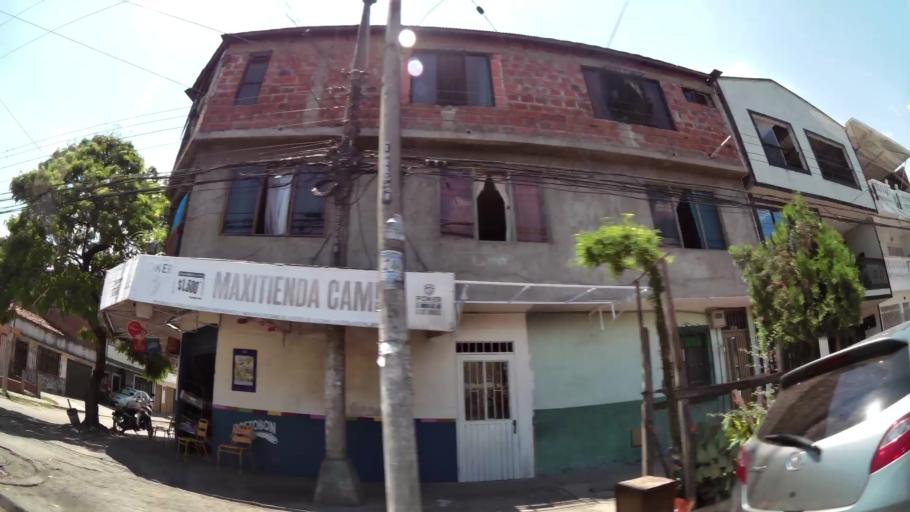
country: CO
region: Valle del Cauca
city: Cali
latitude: 3.4491
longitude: -76.4975
